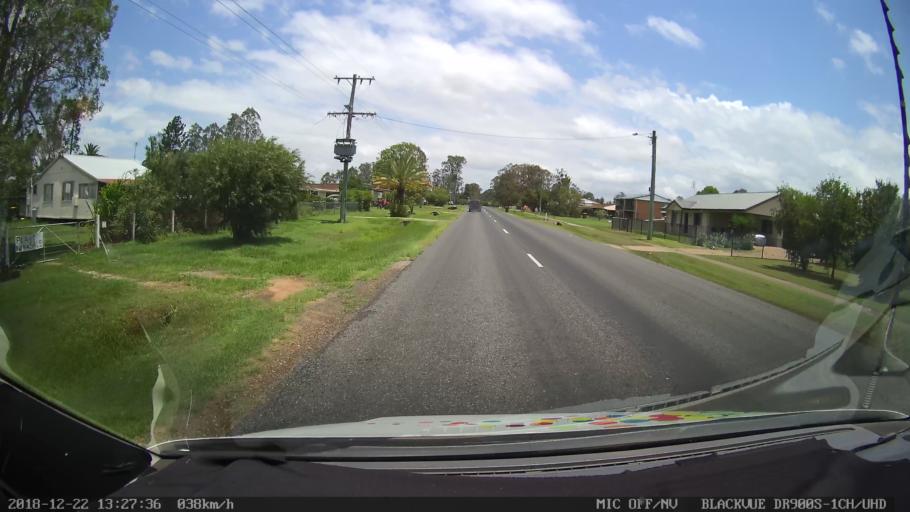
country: AU
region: New South Wales
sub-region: Clarence Valley
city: Coutts Crossing
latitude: -29.8288
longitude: 152.8916
